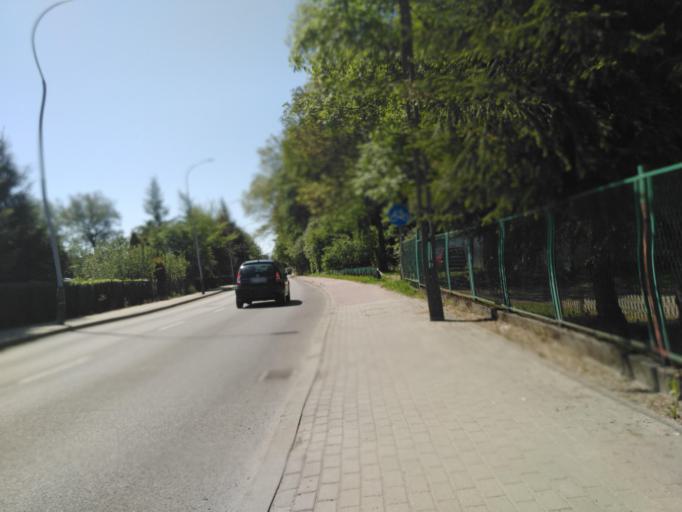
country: PL
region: Subcarpathian Voivodeship
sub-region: Krosno
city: Krosno
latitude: 49.6850
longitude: 21.7857
